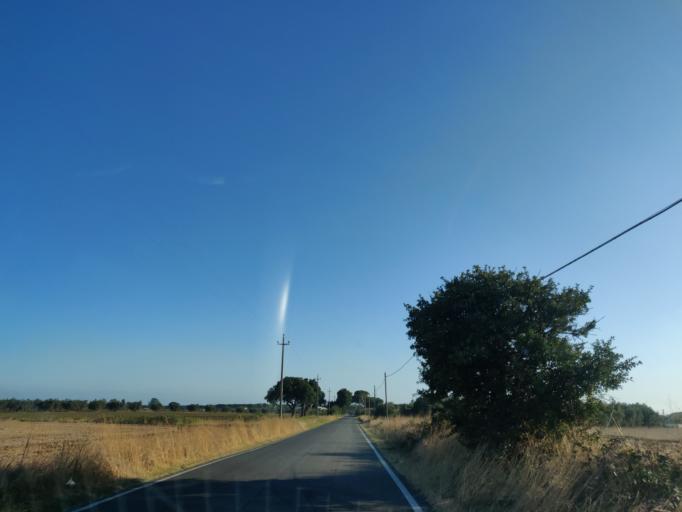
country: IT
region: Latium
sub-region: Provincia di Viterbo
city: Montalto di Castro
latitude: 42.3057
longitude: 11.6521
